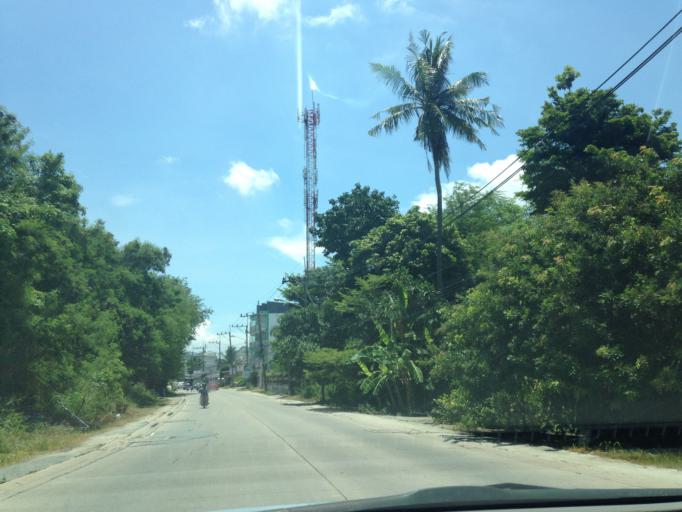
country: TH
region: Chon Buri
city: Chon Buri
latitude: 13.2953
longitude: 100.9367
